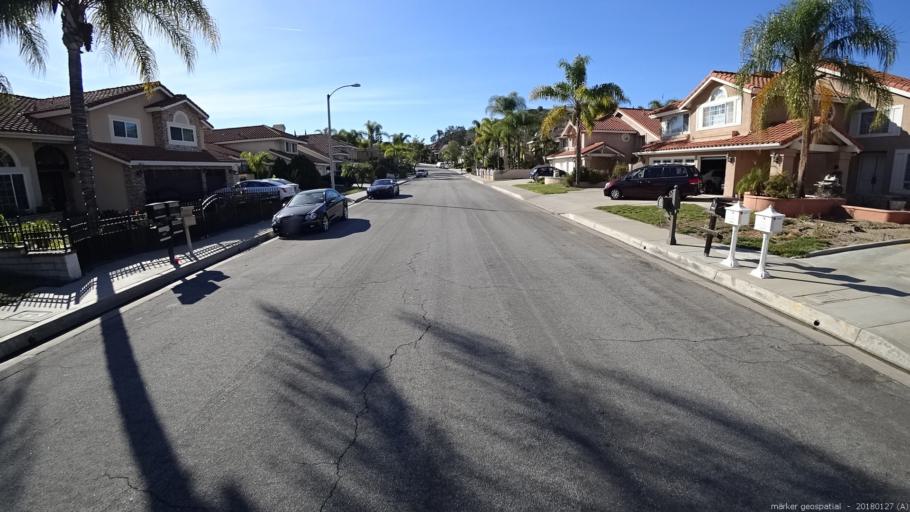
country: US
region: California
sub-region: Los Angeles County
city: Diamond Bar
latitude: 34.0117
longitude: -117.7955
